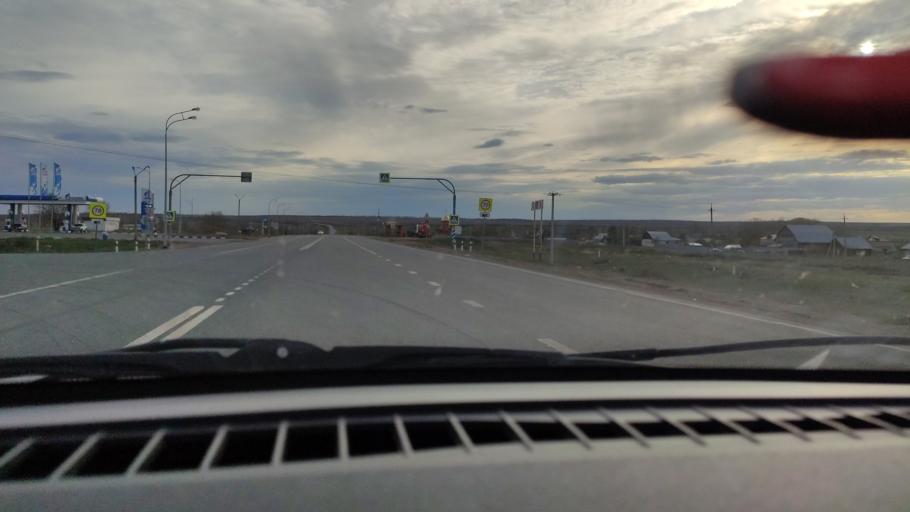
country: RU
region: Orenburg
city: Tatarskaya Kargala
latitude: 52.0278
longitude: 55.2318
